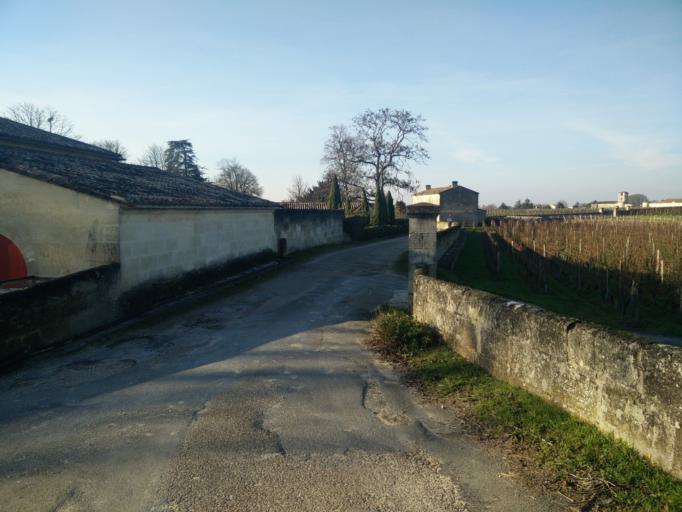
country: FR
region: Aquitaine
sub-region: Departement de la Gironde
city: Saint-Emilion
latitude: 44.8882
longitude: -0.1603
